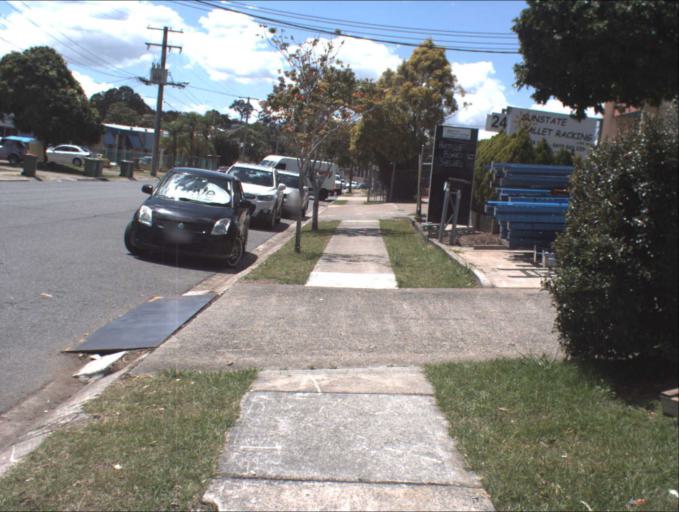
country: AU
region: Queensland
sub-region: Logan
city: Rochedale South
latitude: -27.6065
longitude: 153.1129
